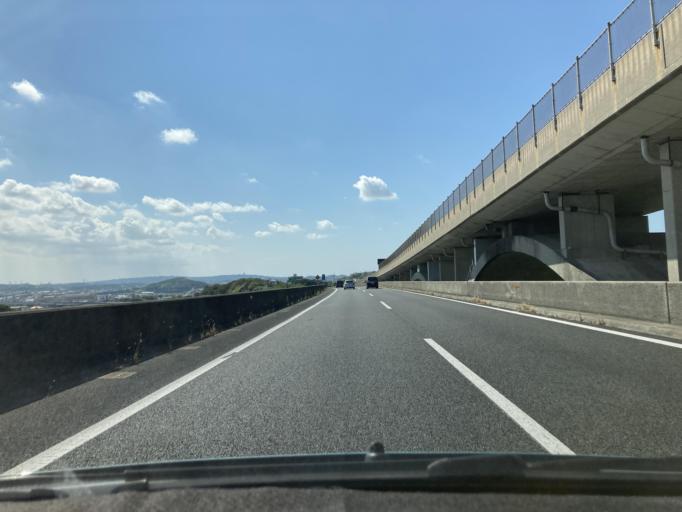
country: JP
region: Okinawa
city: Ginowan
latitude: 26.2141
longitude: 127.7390
